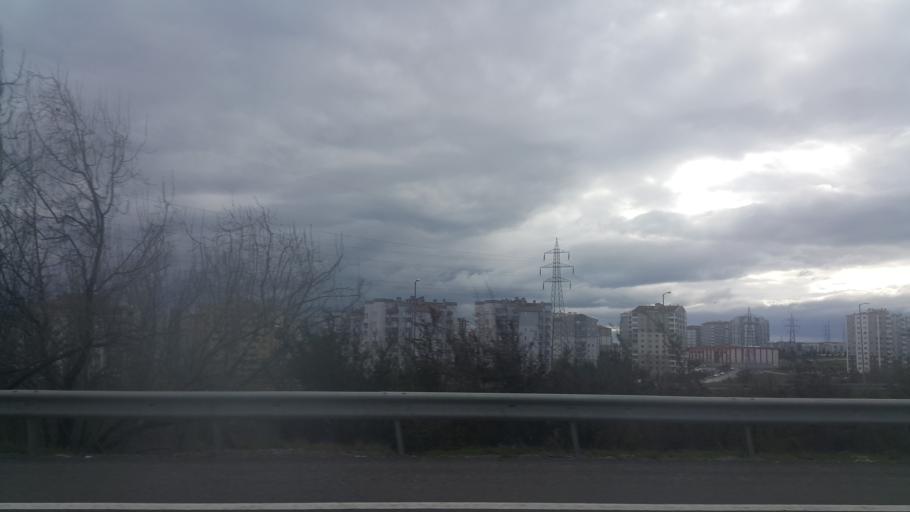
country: TR
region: Ankara
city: Etimesgut
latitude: 40.0034
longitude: 32.6345
